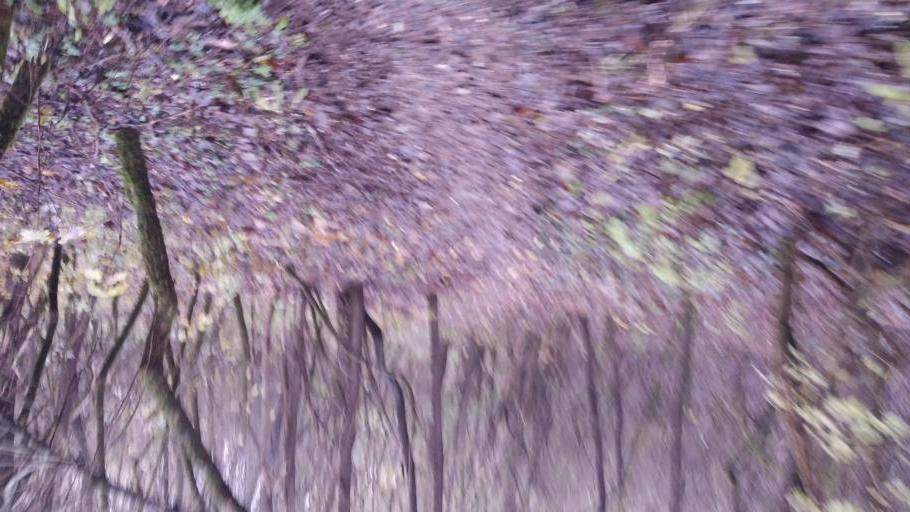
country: HU
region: Pest
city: Pilisszentivan
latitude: 47.6037
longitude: 18.9059
